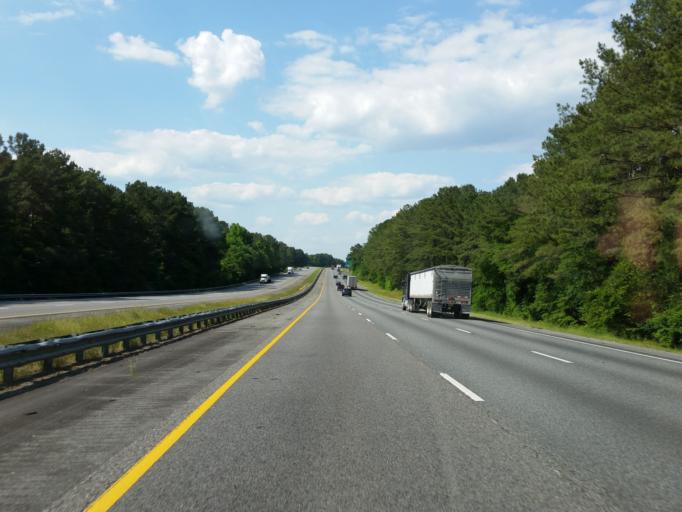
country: US
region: Georgia
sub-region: Houston County
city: Perry
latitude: 32.4045
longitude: -83.7645
